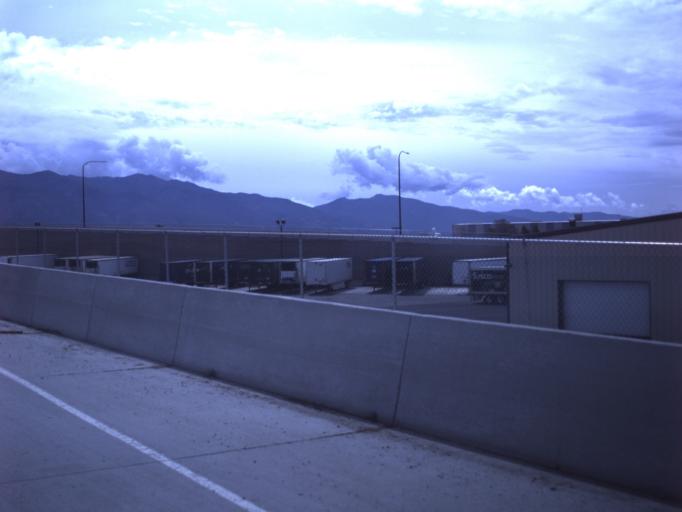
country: US
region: Utah
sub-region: Davis County
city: Clearfield
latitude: 41.1036
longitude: -112.0243
